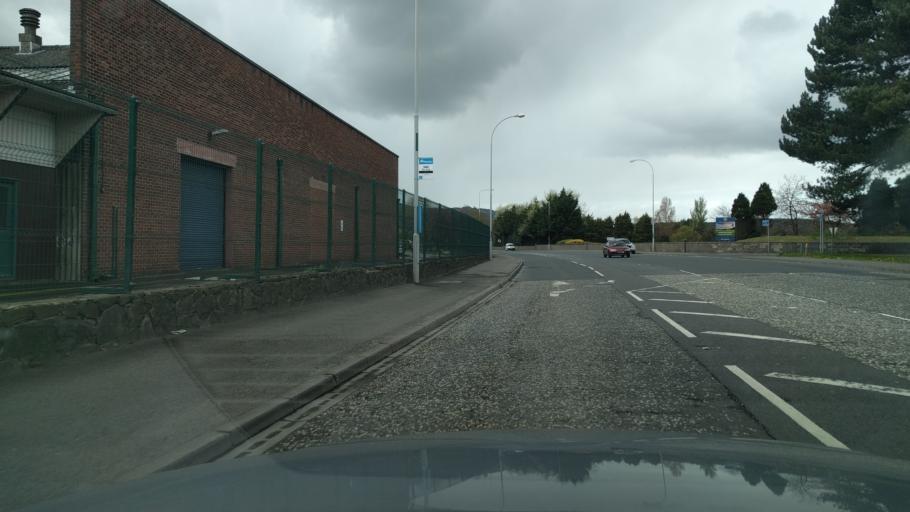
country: GB
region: Northern Ireland
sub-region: Down District
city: Warrenpoint
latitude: 54.1030
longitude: -6.2599
